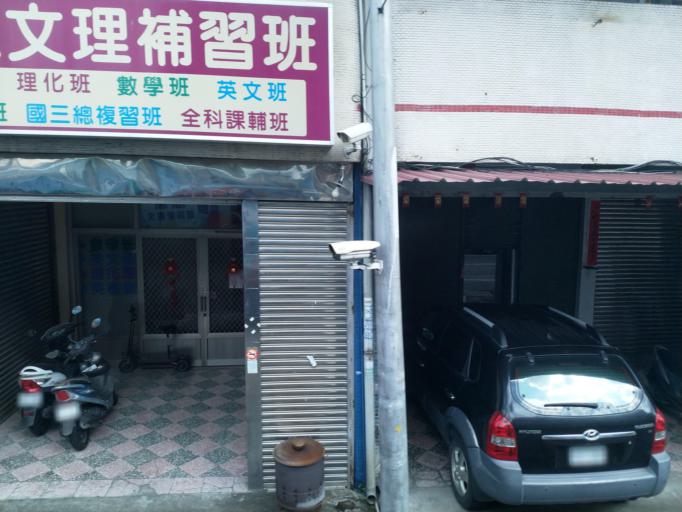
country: TW
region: Taiwan
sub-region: Pingtung
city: Pingtung
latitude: 22.8941
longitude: 120.5494
